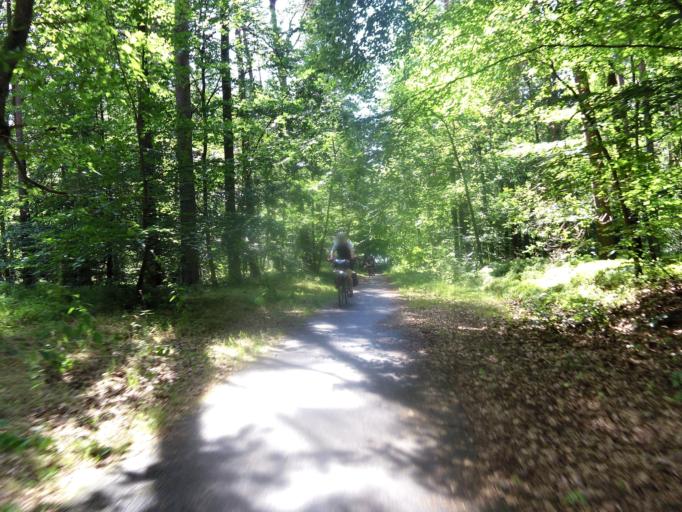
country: DE
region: Brandenburg
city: Lychen
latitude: 53.1908
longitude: 13.2384
